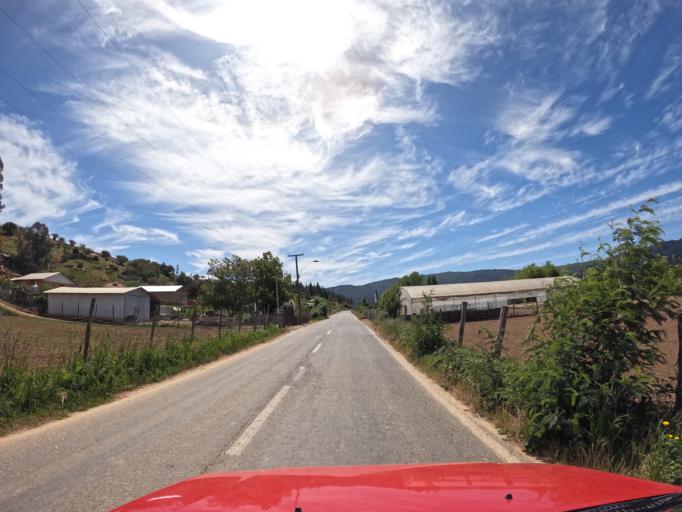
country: CL
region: Maule
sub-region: Provincia de Talca
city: Talca
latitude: -35.0006
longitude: -71.9857
